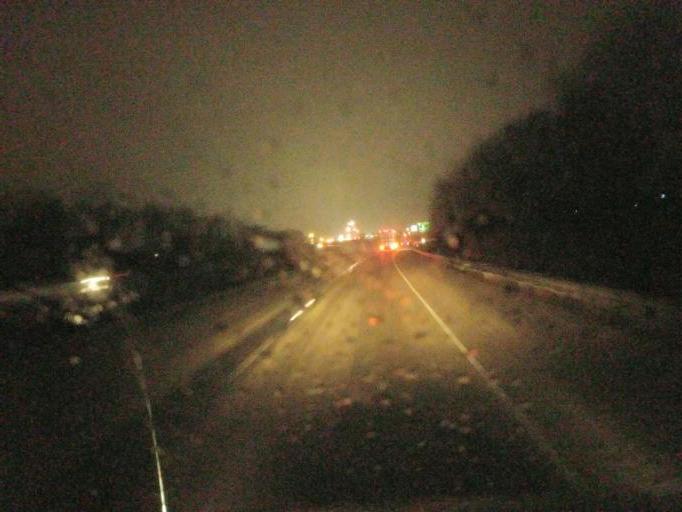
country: US
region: Illinois
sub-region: Fayette County
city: Vandalia
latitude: 38.9772
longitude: -89.0894
